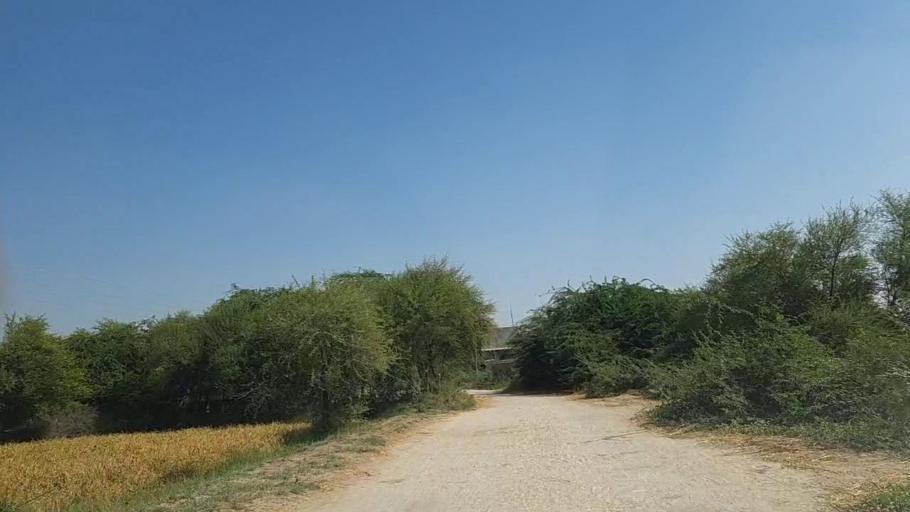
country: PK
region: Sindh
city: Mirpur Batoro
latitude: 24.7325
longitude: 68.2414
